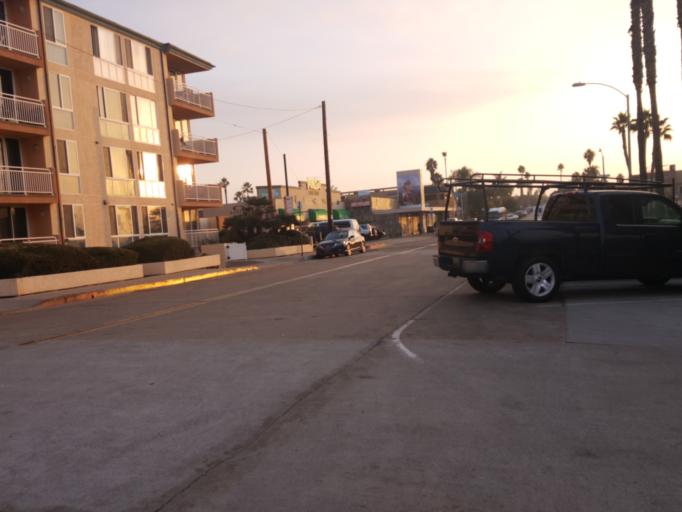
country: US
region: California
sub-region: San Diego County
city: La Jolla
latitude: 32.7971
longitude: -117.2571
